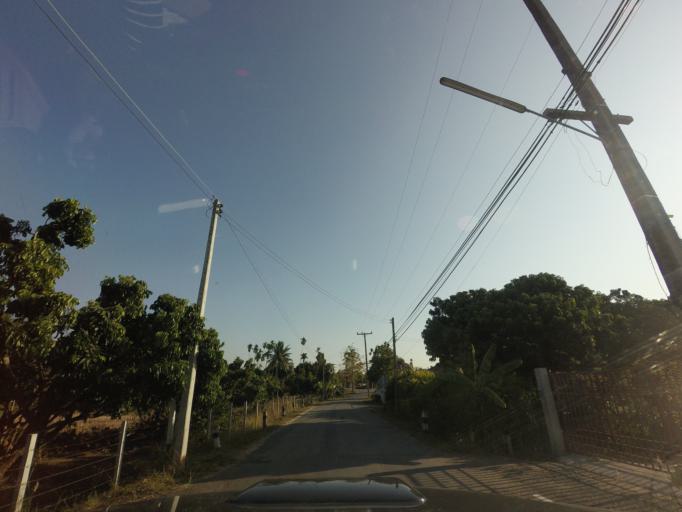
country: TH
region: Chiang Mai
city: San Sai
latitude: 18.9039
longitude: 99.1296
